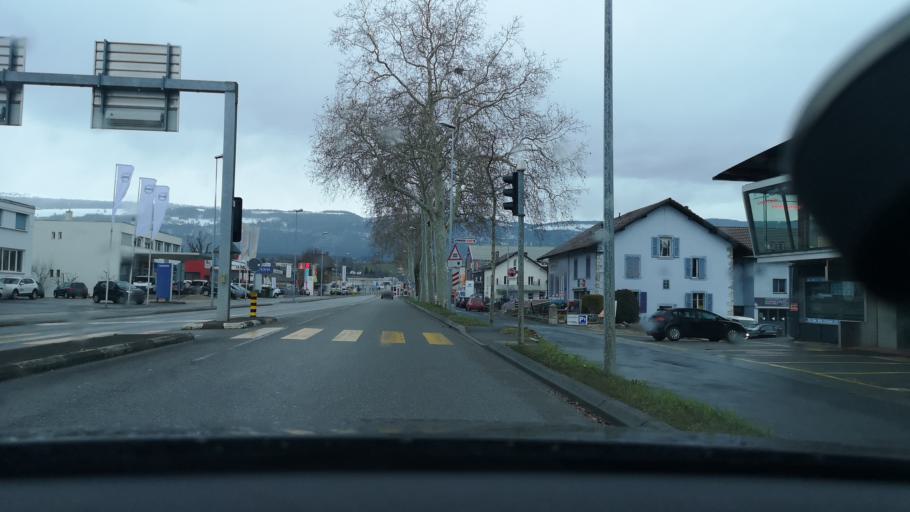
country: CH
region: Vaud
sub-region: Jura-Nord vaudois District
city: Yverdon-les-Bains
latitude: 46.7895
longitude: 6.6296
